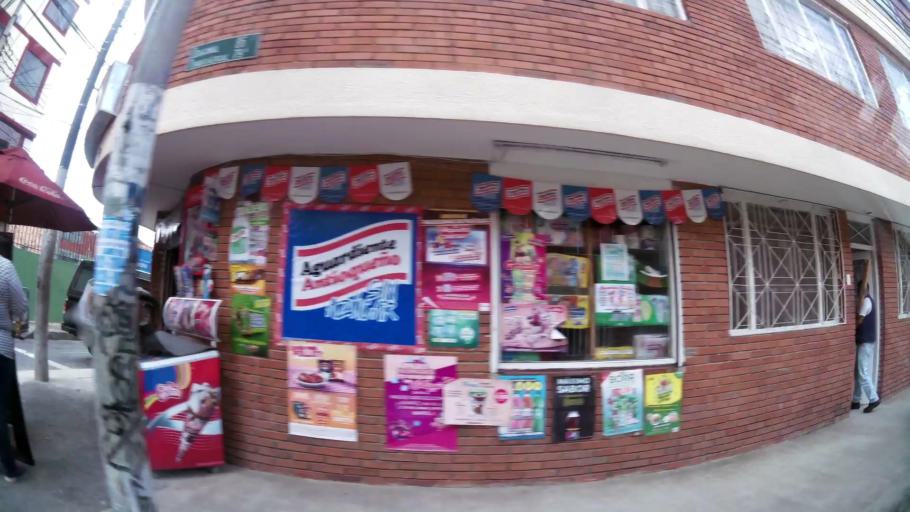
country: CO
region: Bogota D.C.
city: Barrio San Luis
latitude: 4.7071
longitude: -74.0947
